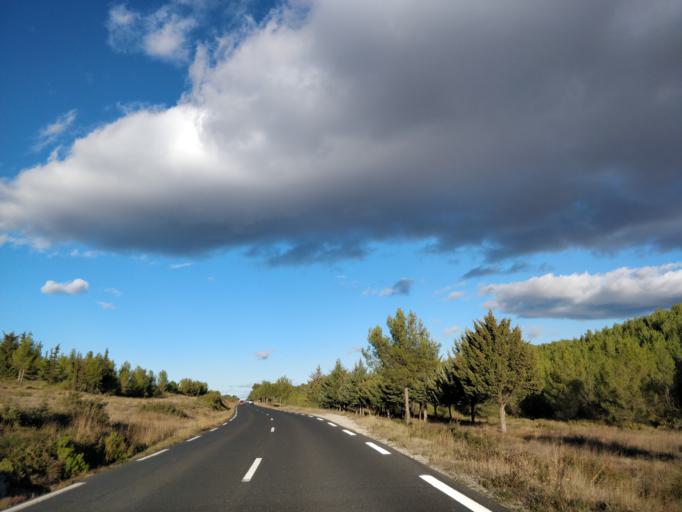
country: FR
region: Languedoc-Roussillon
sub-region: Departement de l'Herault
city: Teyran
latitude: 43.7143
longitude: 3.9460
